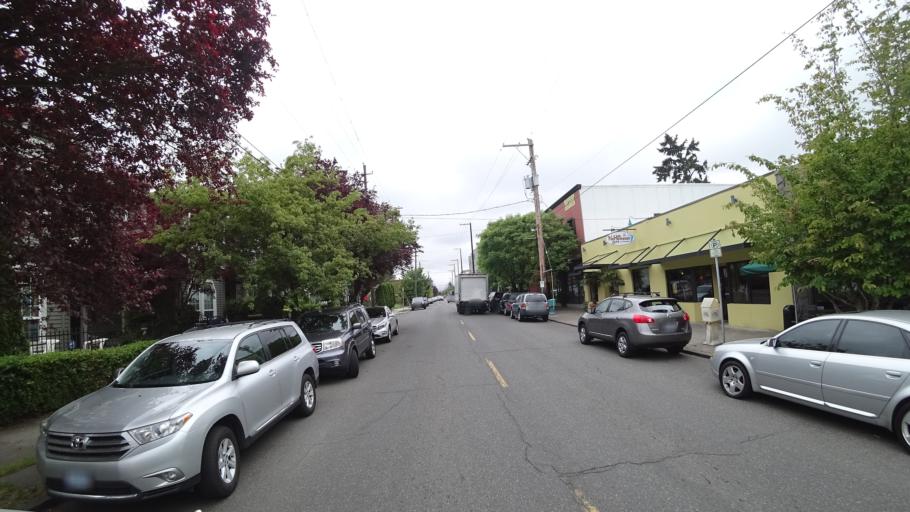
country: US
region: Oregon
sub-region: Multnomah County
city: Portland
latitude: 45.5483
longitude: -122.6153
